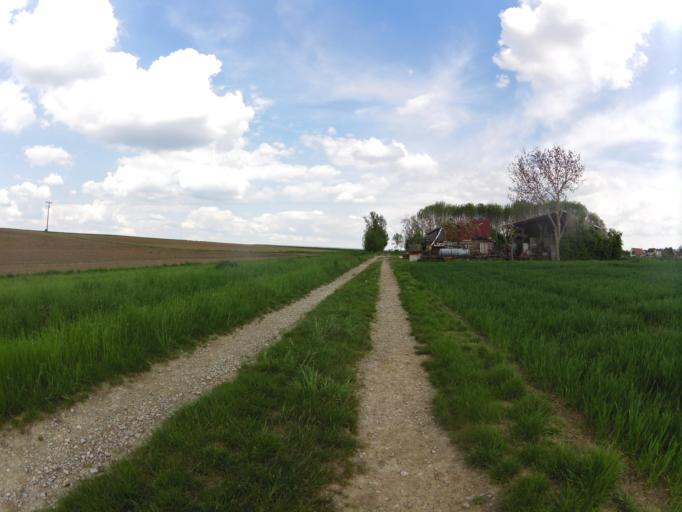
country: DE
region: Bavaria
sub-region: Regierungsbezirk Unterfranken
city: Giebelstadt
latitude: 49.6168
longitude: 9.9439
